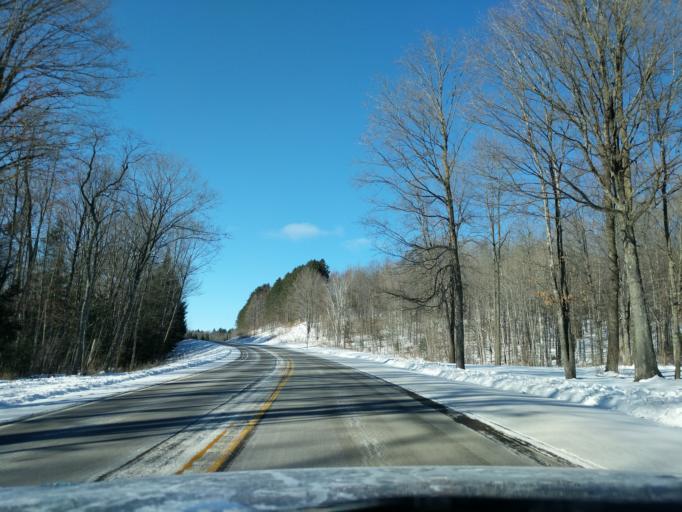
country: US
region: Wisconsin
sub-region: Menominee County
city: Keshena
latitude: 45.1284
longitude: -88.6640
